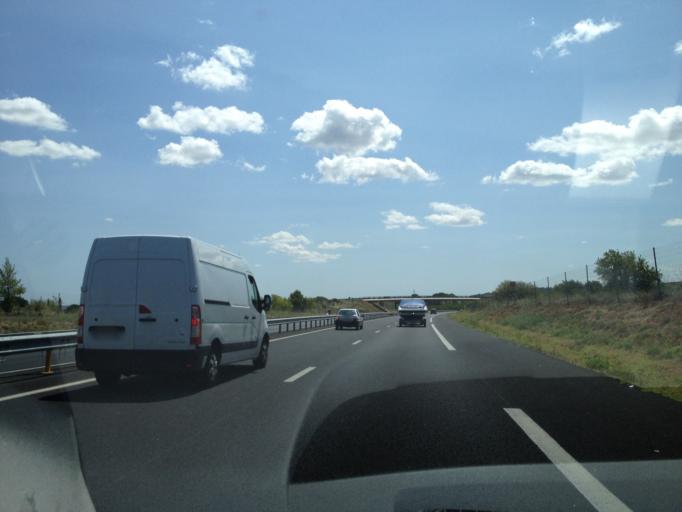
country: FR
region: Languedoc-Roussillon
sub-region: Departement de l'Herault
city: Aspiran
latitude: 43.5807
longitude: 3.4658
